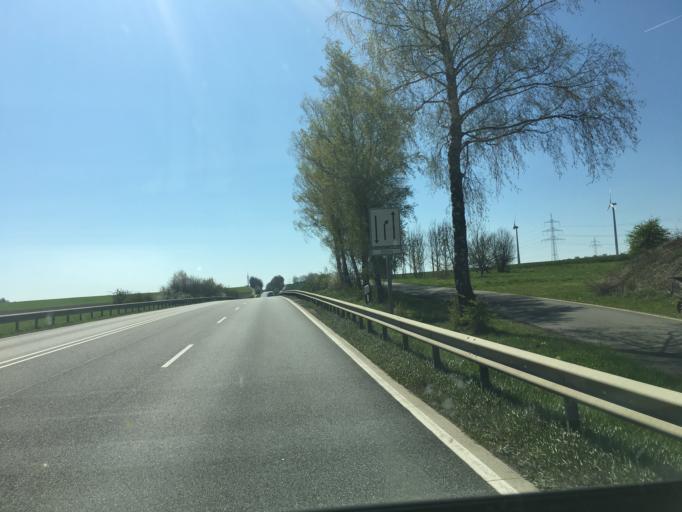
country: DE
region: Rheinland-Pfalz
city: Welschbillig
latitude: 49.8511
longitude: 6.5477
